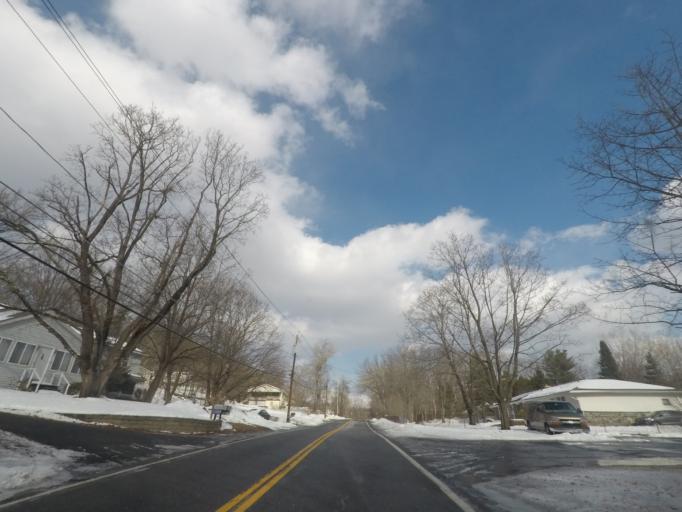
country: US
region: New York
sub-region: Albany County
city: Cohoes
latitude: 42.8122
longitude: -73.7498
